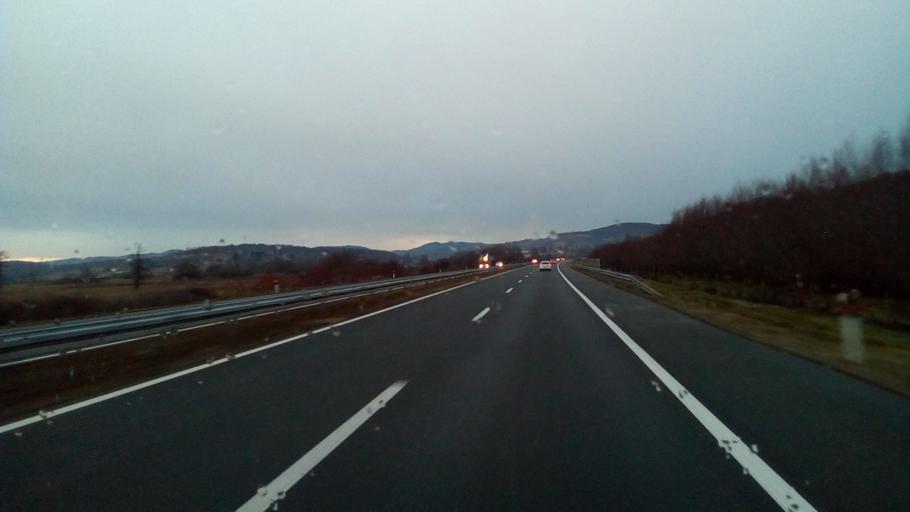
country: HR
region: Varazdinska
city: Remetinec
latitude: 46.0520
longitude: 16.2966
